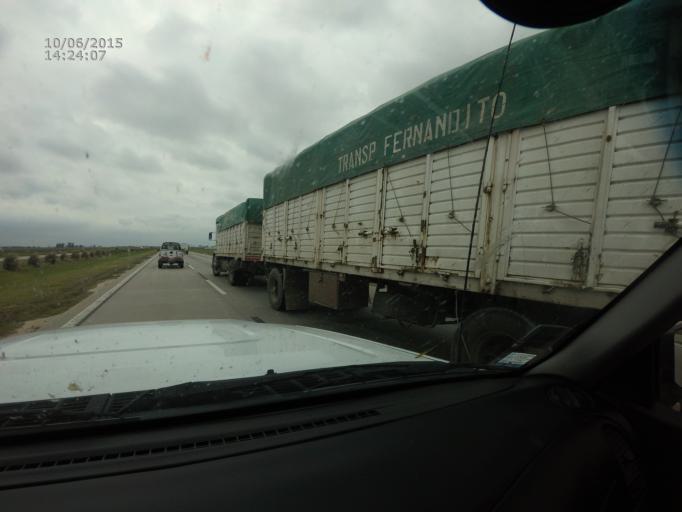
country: AR
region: Cordoba
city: Tio Pujio
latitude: -32.2884
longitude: -63.3001
